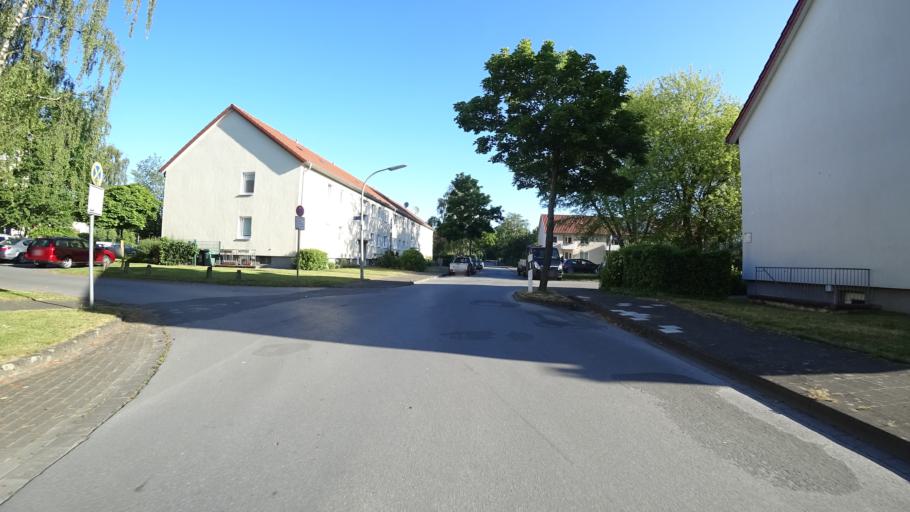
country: DE
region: North Rhine-Westphalia
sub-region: Regierungsbezirk Detmold
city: Rheda-Wiedenbruck
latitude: 51.8455
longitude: 8.2761
